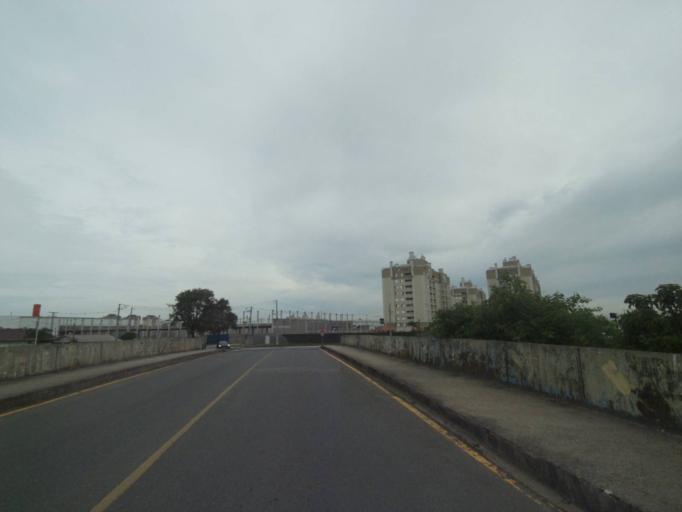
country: BR
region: Parana
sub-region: Pinhais
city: Pinhais
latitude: -25.4286
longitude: -49.2013
